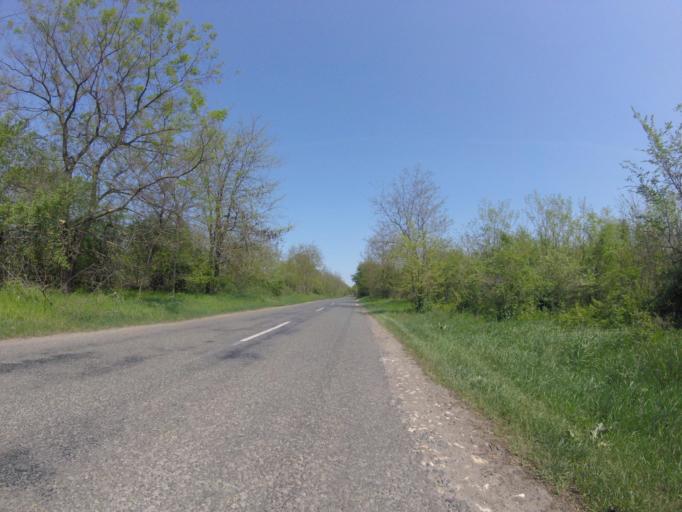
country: HU
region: Pest
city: Danszentmiklos
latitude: 47.1746
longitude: 19.5259
